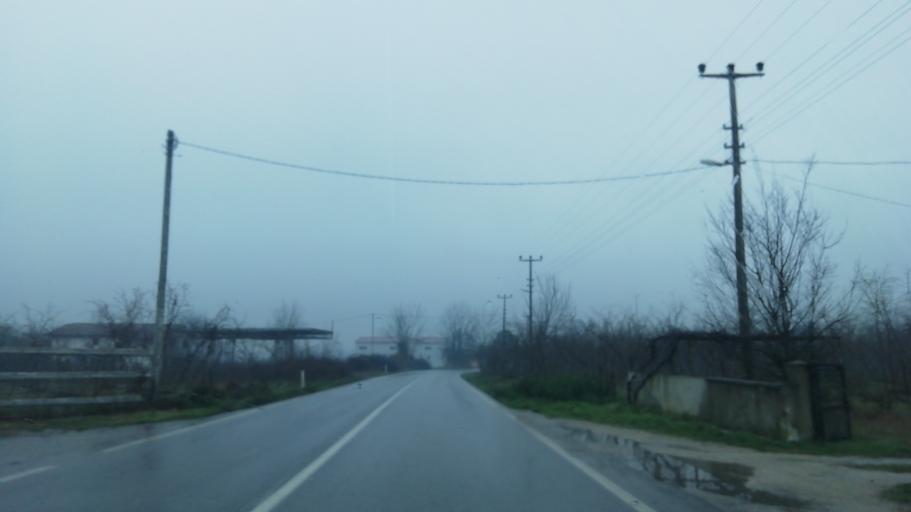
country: TR
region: Sakarya
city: Karapurcek
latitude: 40.6898
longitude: 30.4727
